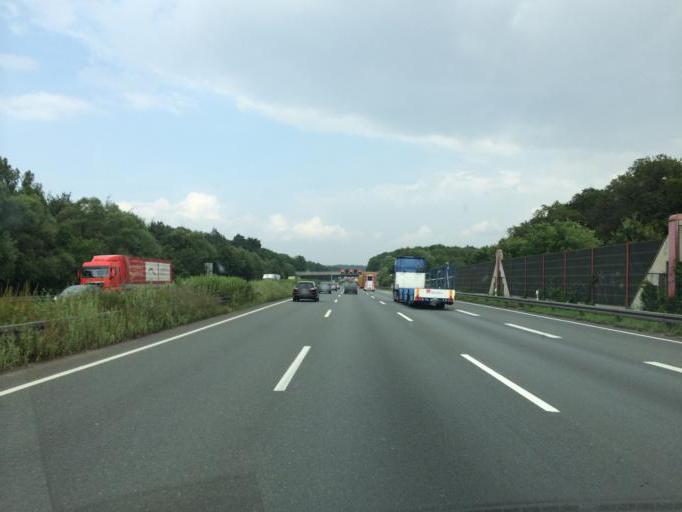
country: DE
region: Lower Saxony
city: Gross Munzel
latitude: 52.4096
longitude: 9.5106
